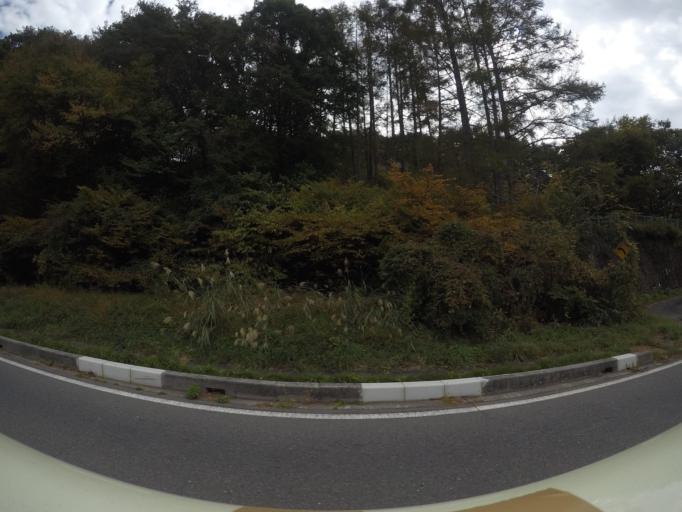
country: JP
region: Nagano
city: Chino
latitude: 35.9310
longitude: 138.0980
